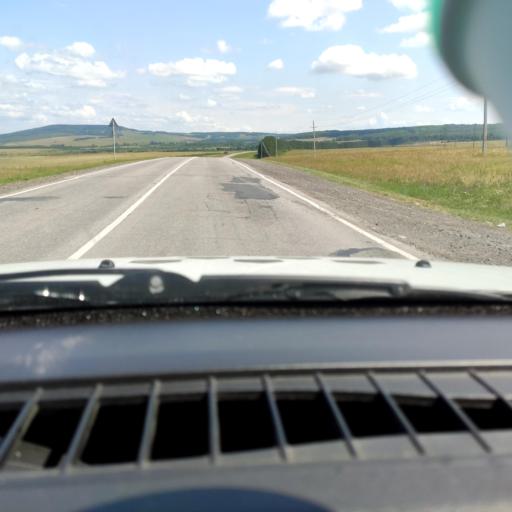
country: RU
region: Bashkortostan
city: Verkhniye Kigi
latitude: 55.3972
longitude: 58.6283
